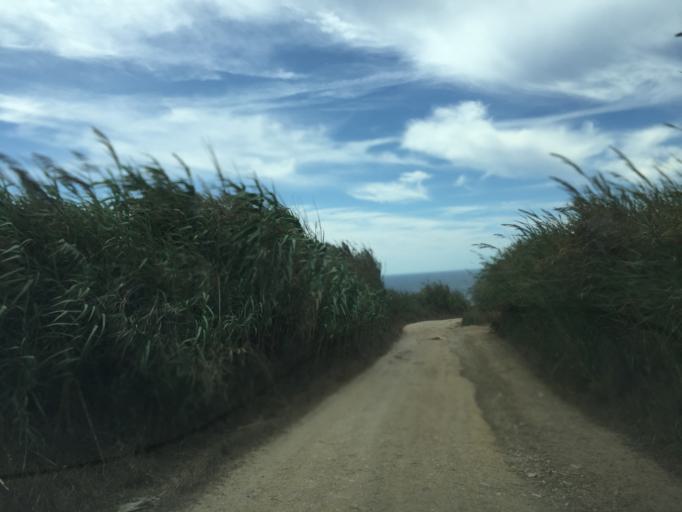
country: PT
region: Lisbon
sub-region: Lourinha
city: Lourinha
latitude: 39.1917
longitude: -9.3424
